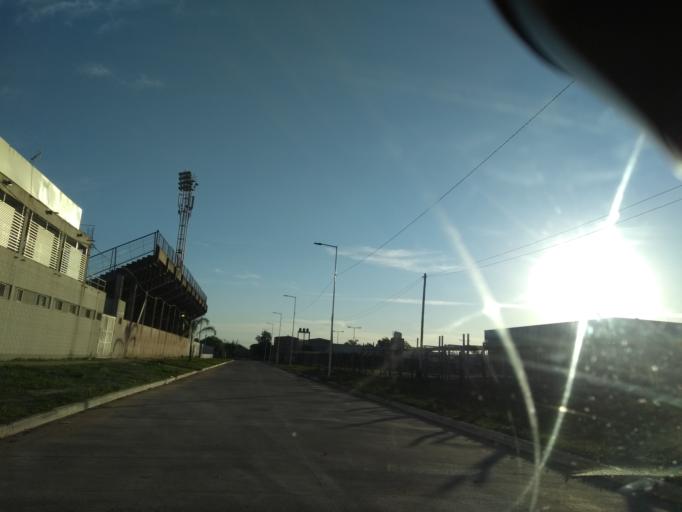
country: AR
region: Chaco
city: Resistencia
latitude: -27.4692
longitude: -58.9672
